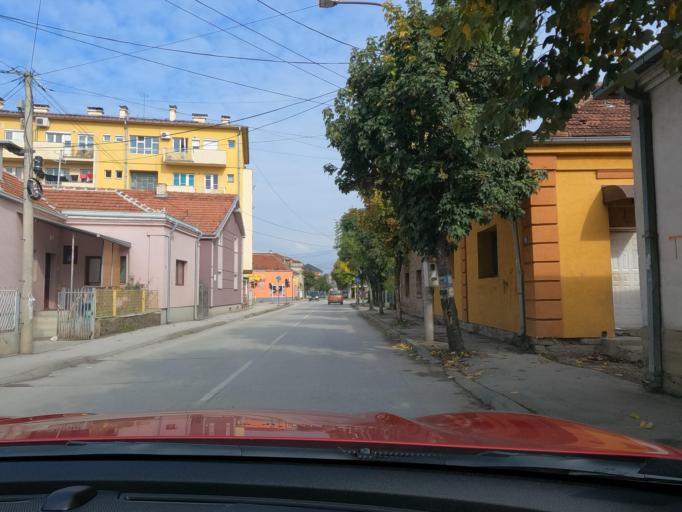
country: RS
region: Central Serbia
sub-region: Moravicki Okrug
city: Cacak
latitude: 43.8865
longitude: 20.3442
